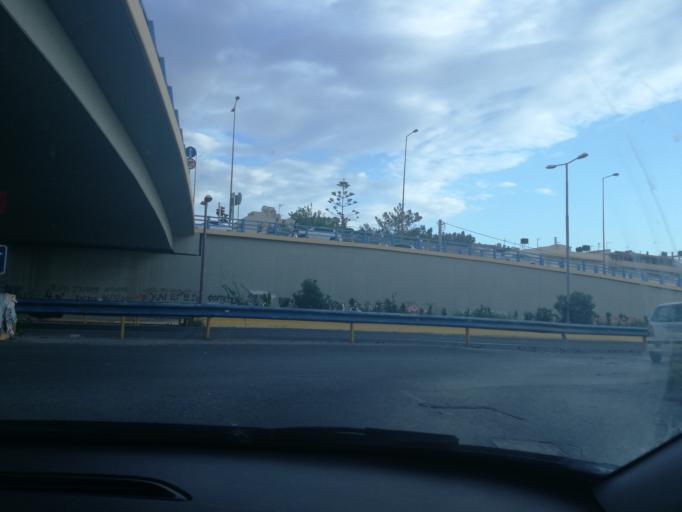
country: GR
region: Crete
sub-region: Nomos Irakleiou
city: Irakleion
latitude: 35.3201
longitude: 25.1400
